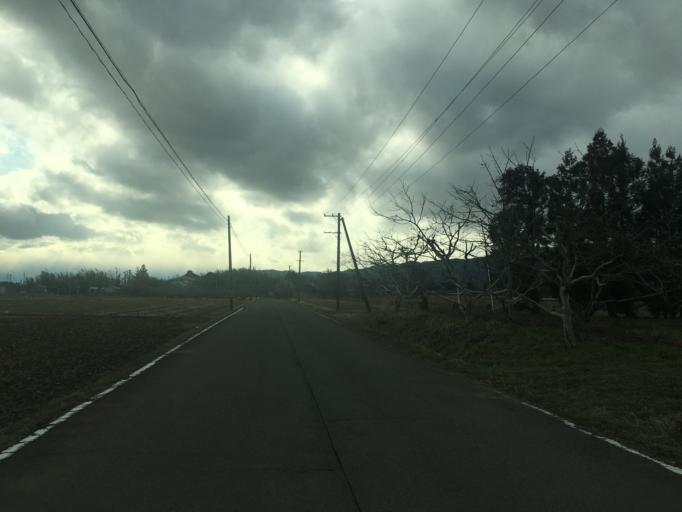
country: JP
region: Fukushima
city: Yanagawamachi-saiwaicho
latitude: 37.8866
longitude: 140.5891
